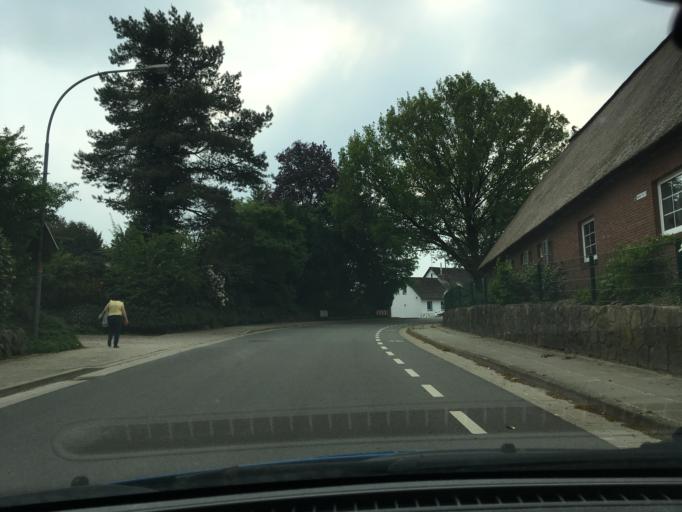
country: DE
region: Lower Saxony
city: Buchholz in der Nordheide
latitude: 53.4053
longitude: 9.8837
